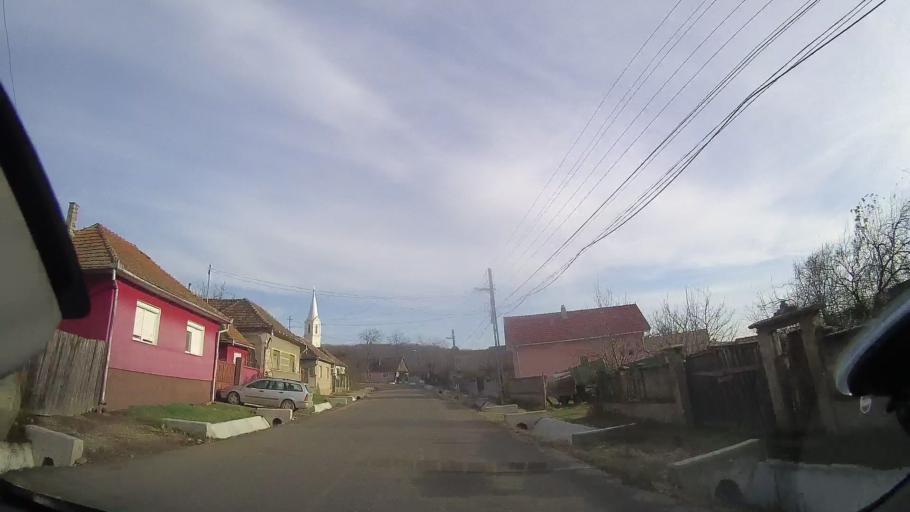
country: RO
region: Bihor
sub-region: Comuna Sarbi
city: Burzuc
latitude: 47.1765
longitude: 22.1490
